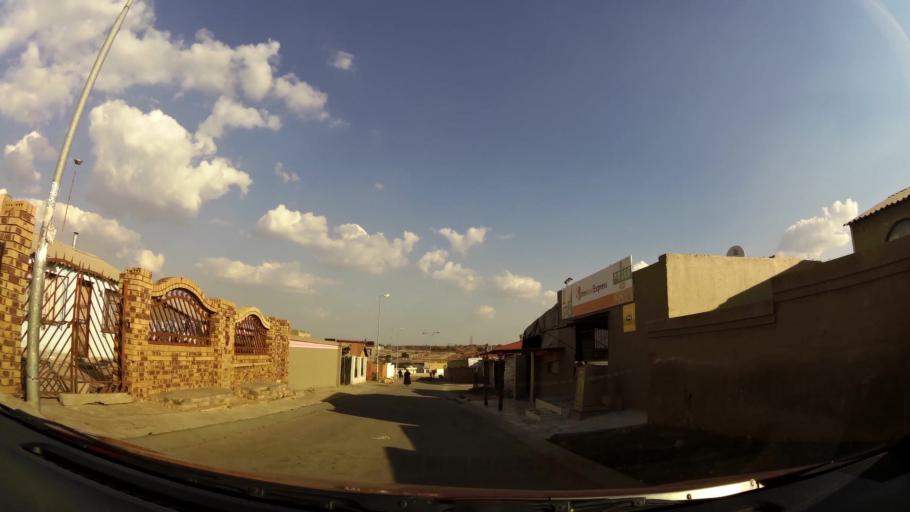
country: ZA
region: Gauteng
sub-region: City of Johannesburg Metropolitan Municipality
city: Soweto
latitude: -26.2344
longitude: 27.8639
